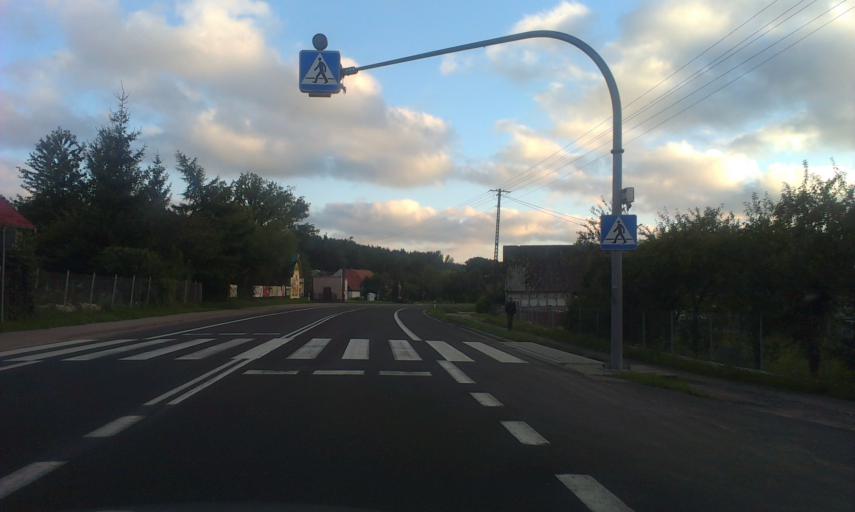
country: PL
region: West Pomeranian Voivodeship
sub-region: Powiat koszalinski
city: Sianow
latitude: 54.2718
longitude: 16.4265
